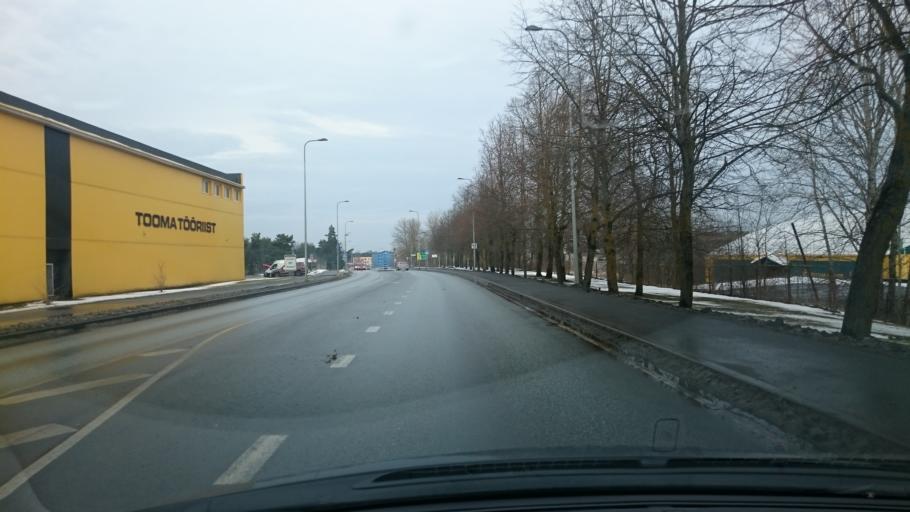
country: EE
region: Harju
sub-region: Tallinna linn
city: Tallinn
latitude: 59.3674
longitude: 24.7179
